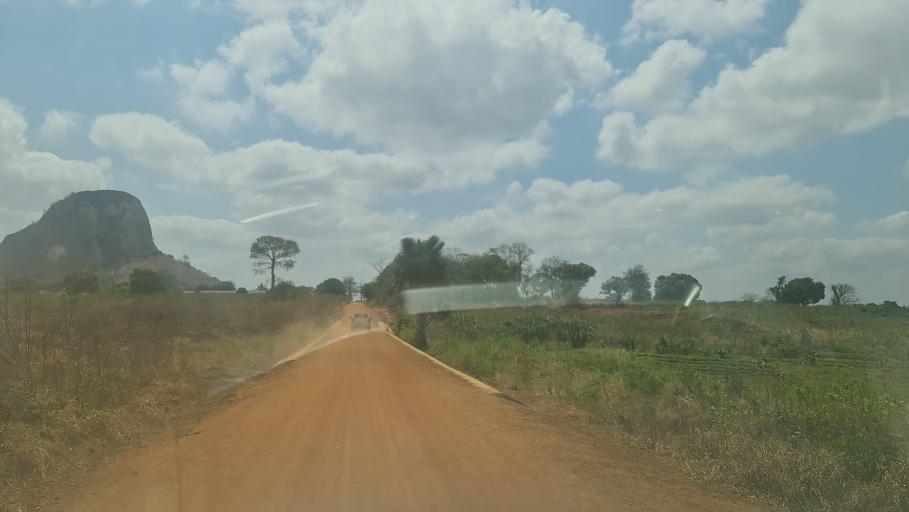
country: MW
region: Southern Region
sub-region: Nsanje District
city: Nsanje
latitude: -17.3953
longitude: 35.5686
